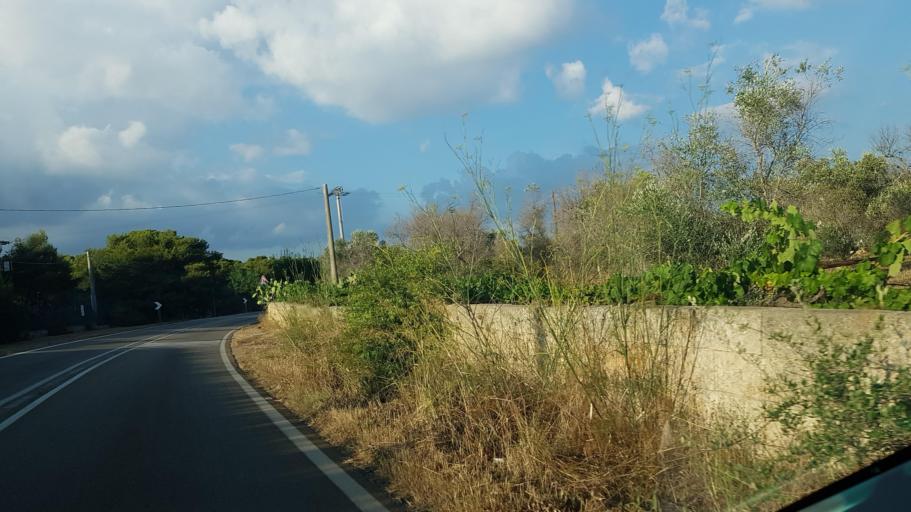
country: IT
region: Apulia
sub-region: Provincia di Lecce
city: Gemini
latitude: 39.8659
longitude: 18.2097
